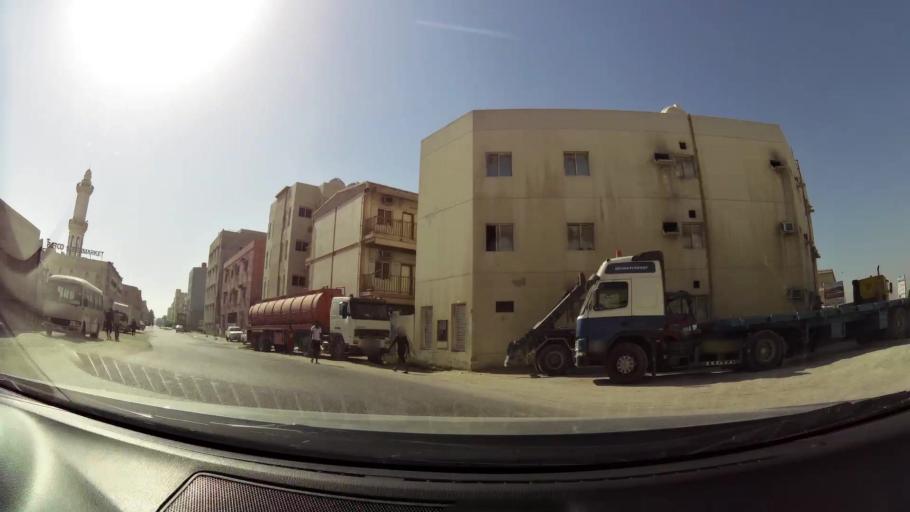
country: AE
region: Dubai
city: Dubai
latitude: 25.0087
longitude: 55.1114
